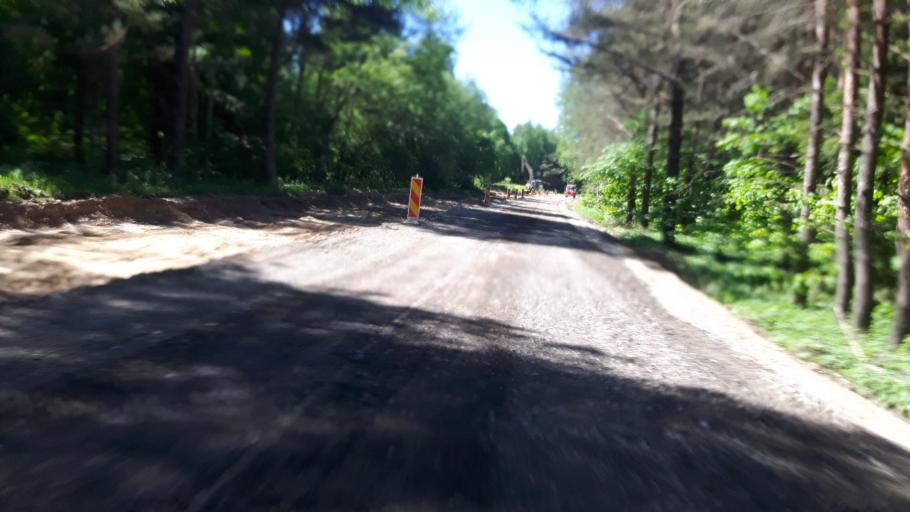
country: EE
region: Ida-Virumaa
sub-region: Narva-Joesuu linn
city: Narva-Joesuu
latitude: 59.4198
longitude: 27.9750
